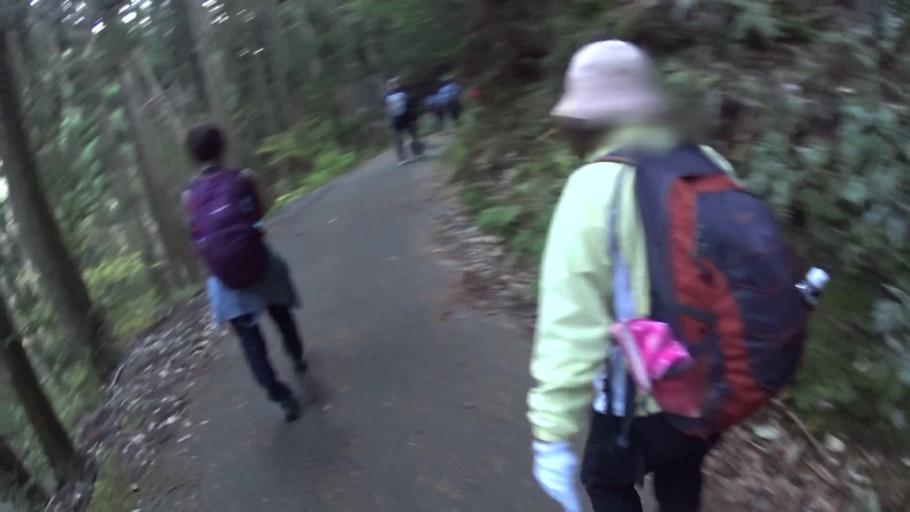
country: JP
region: Kyoto
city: Kameoka
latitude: 35.0503
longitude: 135.6519
